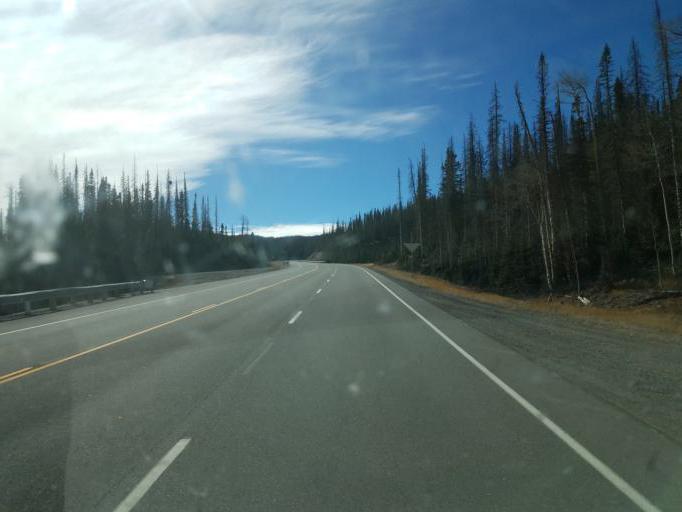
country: US
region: Colorado
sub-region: Archuleta County
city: Pagosa Springs
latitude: 37.4870
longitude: -106.7678
